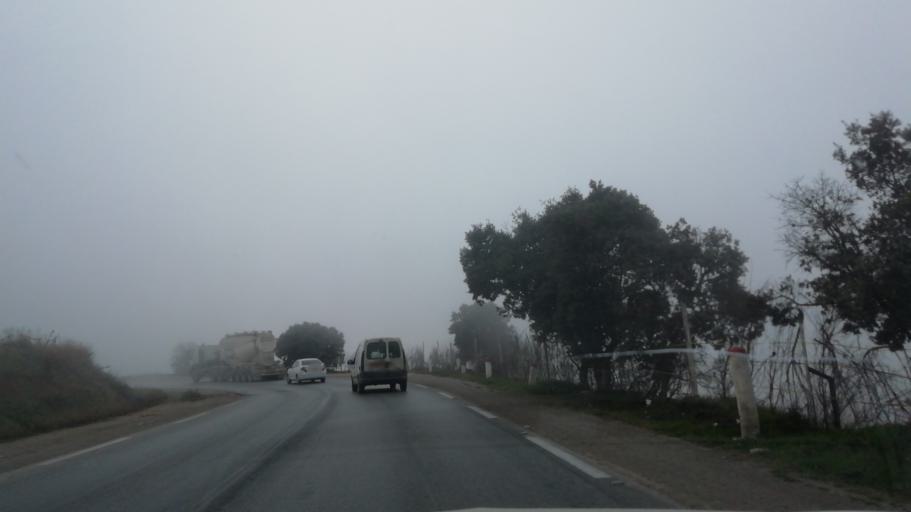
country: DZ
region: Mascara
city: Mascara
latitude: 35.5263
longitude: 0.3248
